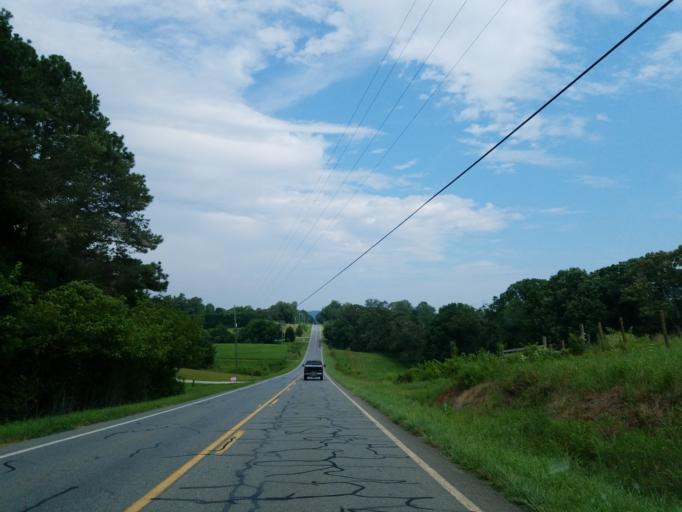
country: US
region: Georgia
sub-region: Gilmer County
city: Ellijay
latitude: 34.6437
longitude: -84.5509
